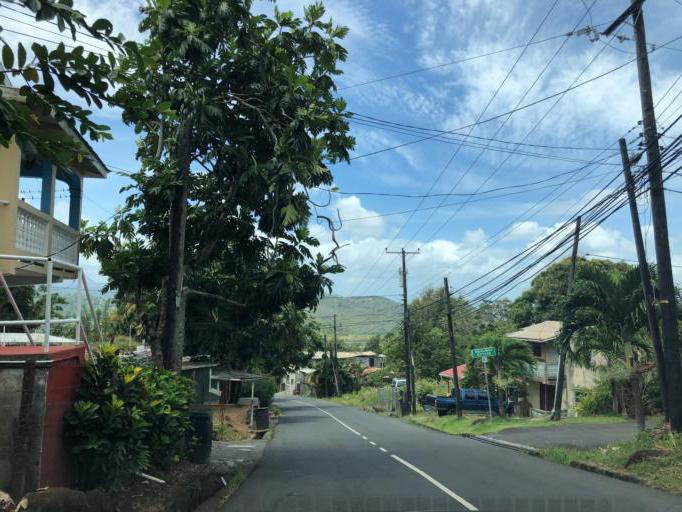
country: LC
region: Castries Quarter
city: Castries
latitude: 13.9979
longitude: -61.0028
